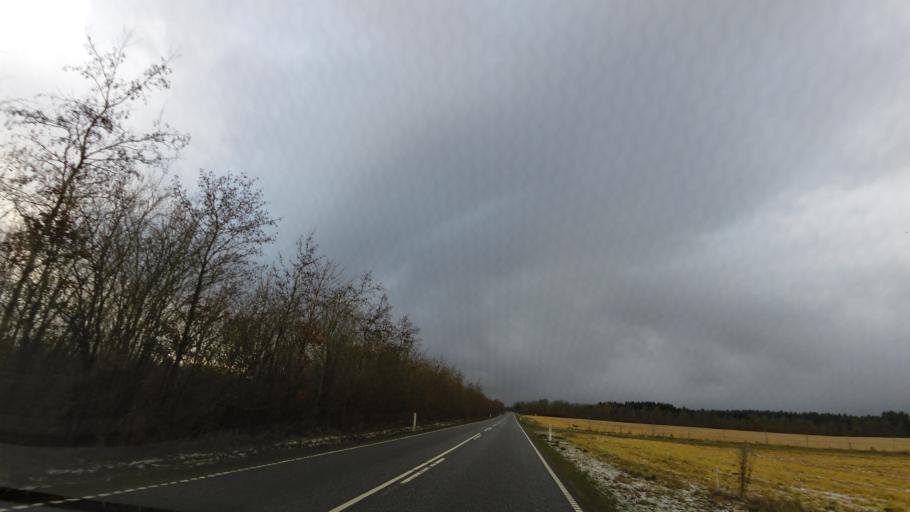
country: DK
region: Central Jutland
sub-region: Ikast-Brande Kommune
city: Brande
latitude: 55.9865
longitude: 9.2407
